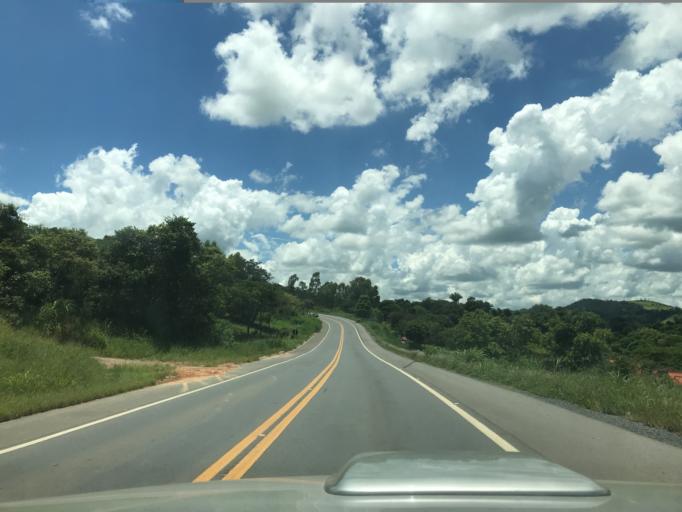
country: BR
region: Minas Gerais
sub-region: Perdoes
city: Perdoes
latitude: -21.0896
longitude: -45.0984
